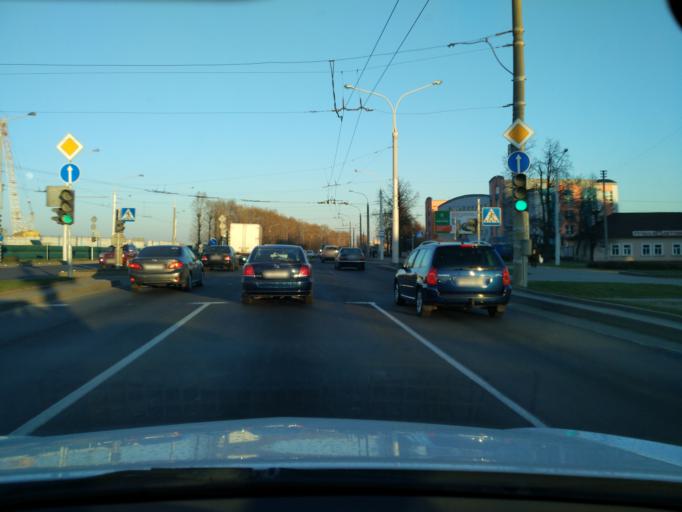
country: BY
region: Minsk
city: Syenitsa
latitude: 53.8678
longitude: 27.5253
